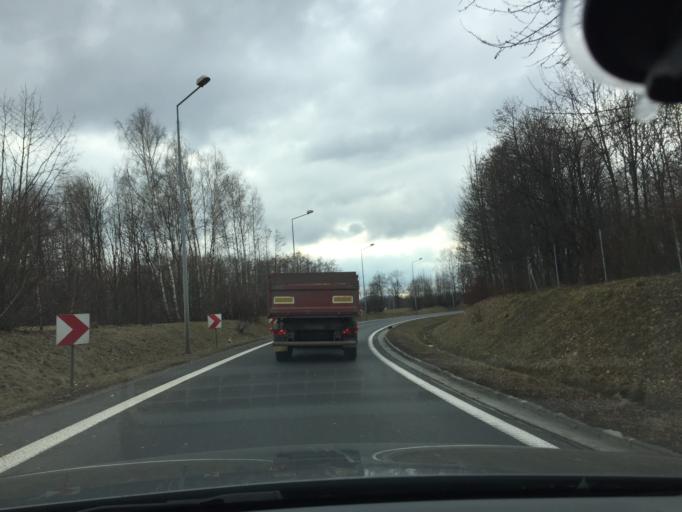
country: PL
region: Silesian Voivodeship
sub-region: Bielsko-Biala
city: Bielsko-Biala
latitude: 49.8502
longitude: 19.0285
